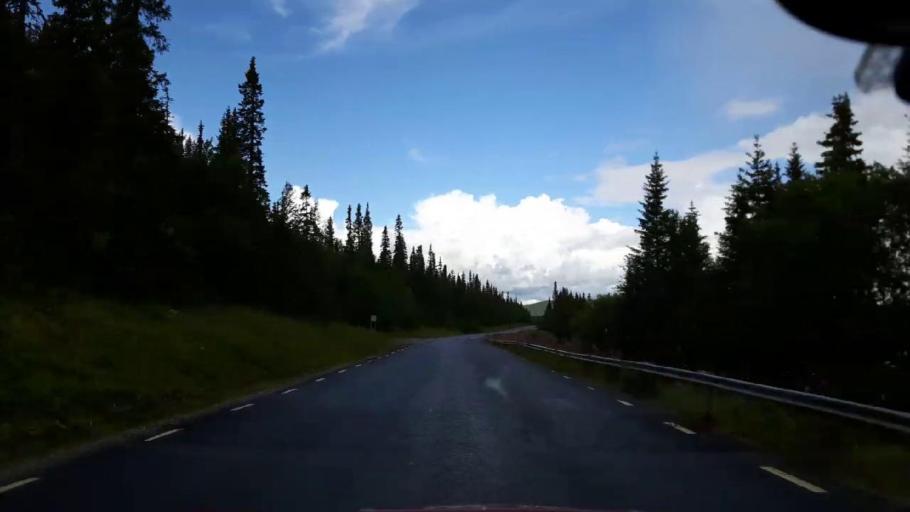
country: SE
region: Vaesterbotten
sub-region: Vilhelmina Kommun
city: Sjoberg
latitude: 65.0016
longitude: 15.1961
